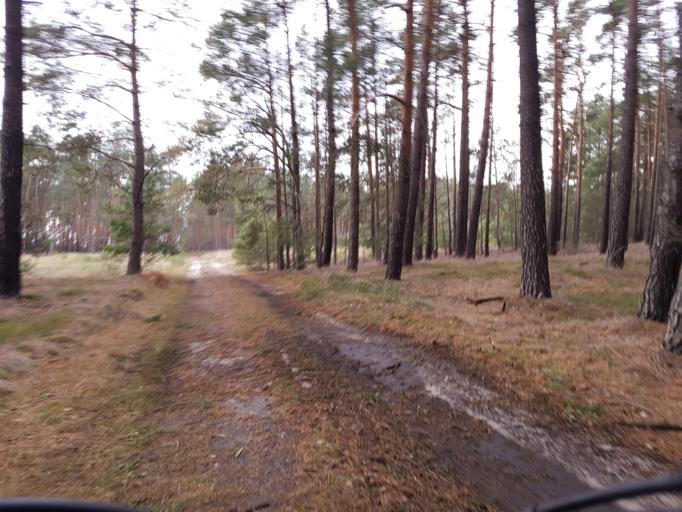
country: DE
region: Brandenburg
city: Schilda
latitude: 51.6182
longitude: 13.3698
